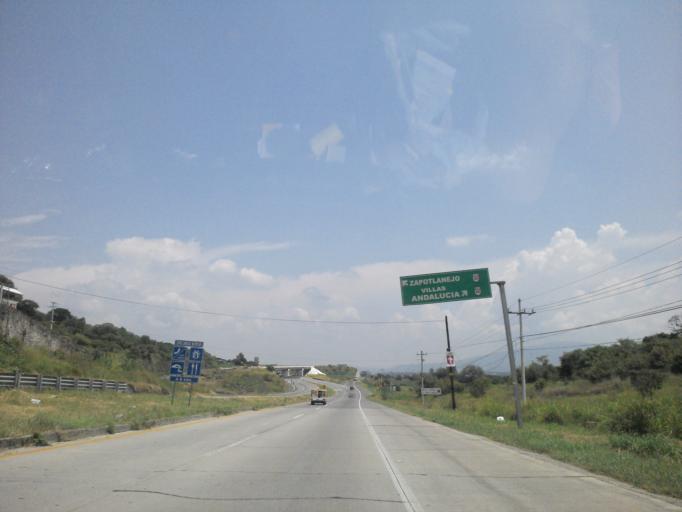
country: MX
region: Jalisco
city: Puente Grande
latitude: 20.5741
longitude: -103.1717
